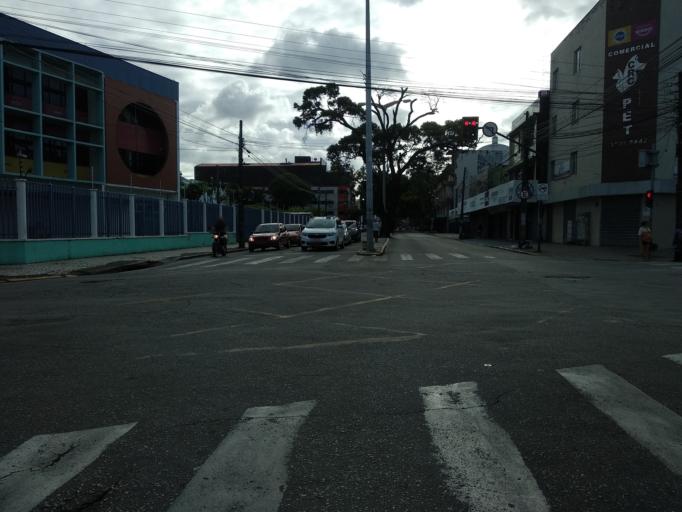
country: BR
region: Ceara
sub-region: Fortaleza
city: Fortaleza
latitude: -3.7335
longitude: -38.5245
